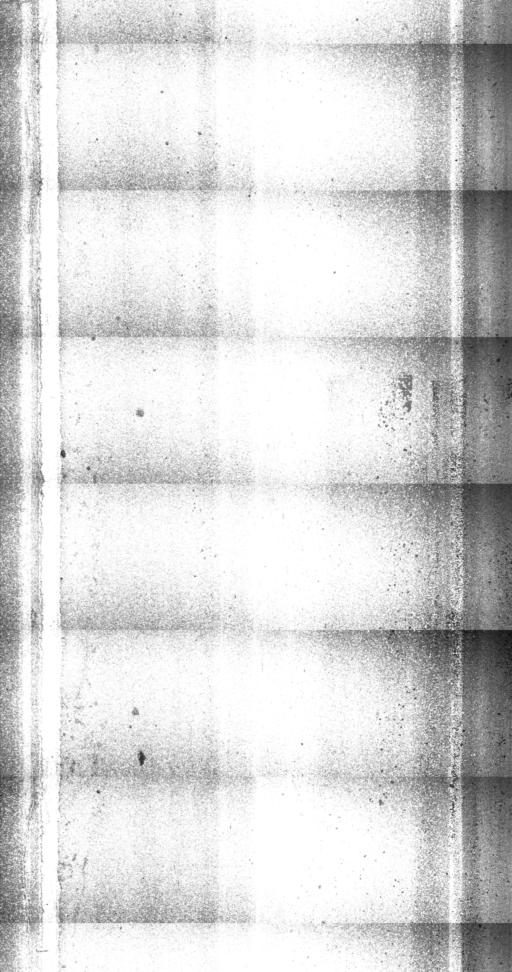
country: US
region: Vermont
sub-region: Chittenden County
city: Jericho
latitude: 44.5391
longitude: -72.9491
